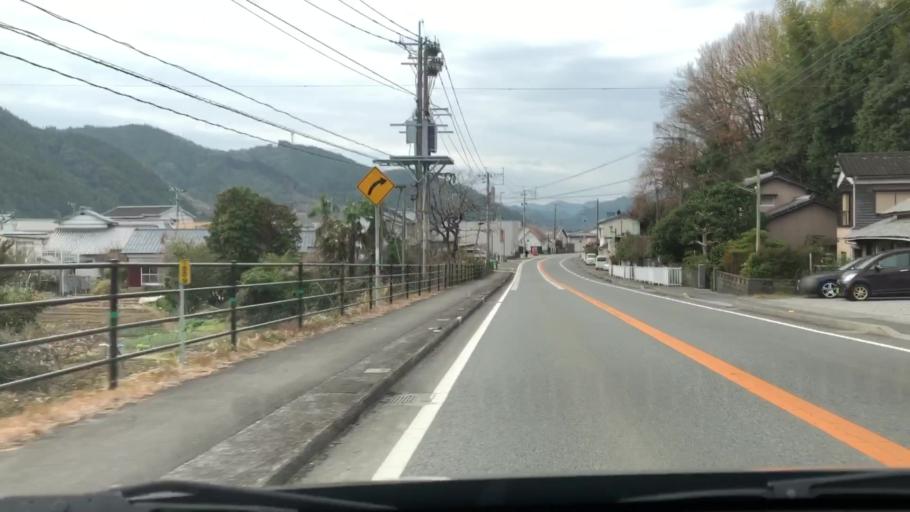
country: JP
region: Oita
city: Saiki
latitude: 32.9794
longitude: 131.8468
